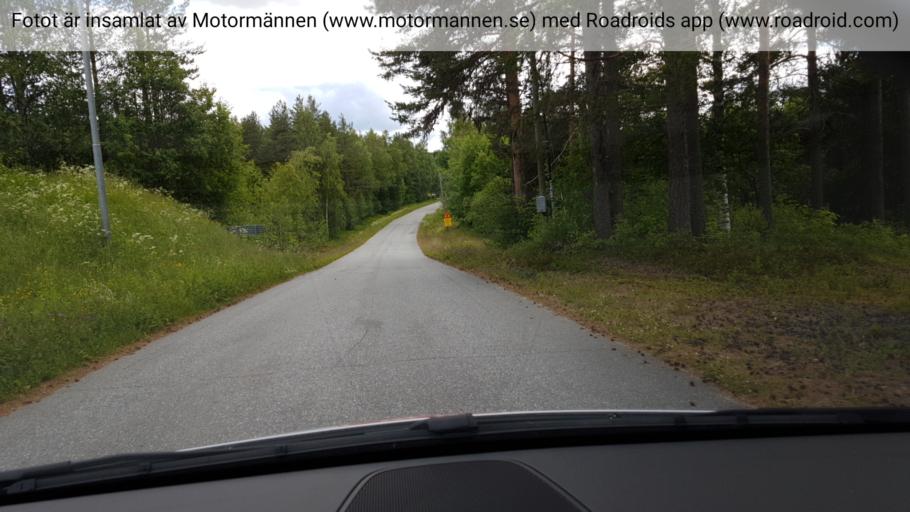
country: SE
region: Vaesterbotten
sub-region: Dorotea Kommun
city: Dorotea
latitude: 63.9205
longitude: 16.3362
